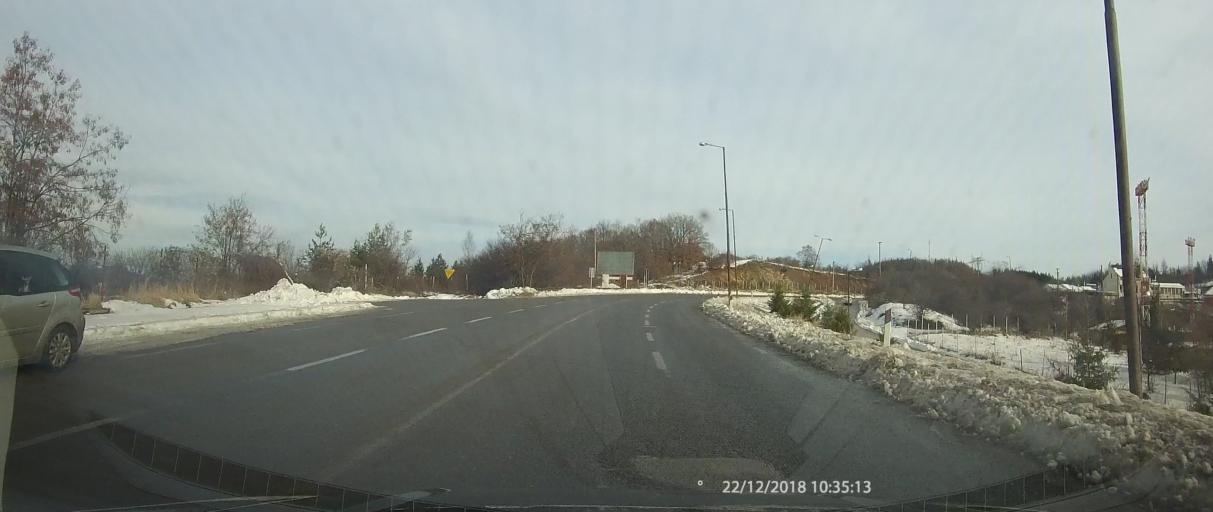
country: MK
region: Kriva Palanka
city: Kriva Palanka
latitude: 42.2201
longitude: 22.4558
